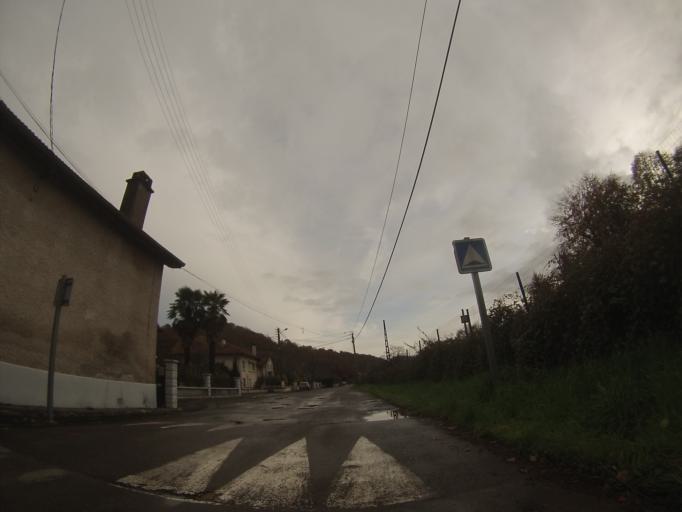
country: FR
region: Aquitaine
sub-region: Departement des Pyrenees-Atlantiques
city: Jurancon
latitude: 43.2775
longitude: -0.3871
